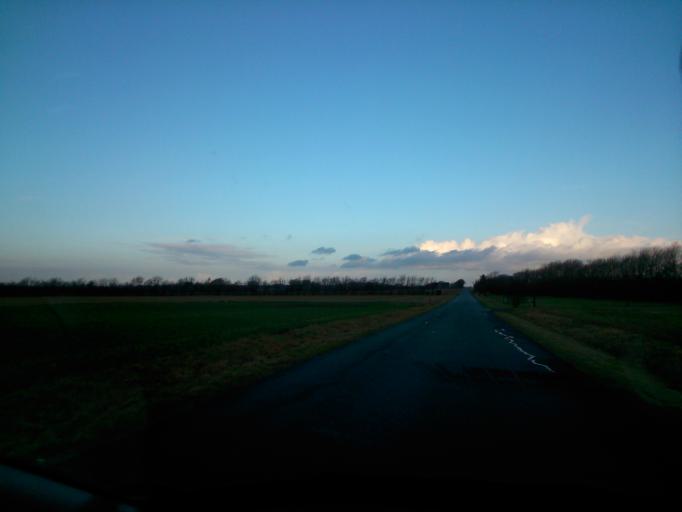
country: DK
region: Central Jutland
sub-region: Ringkobing-Skjern Kommune
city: Videbaek
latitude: 56.0463
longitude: 8.5710
